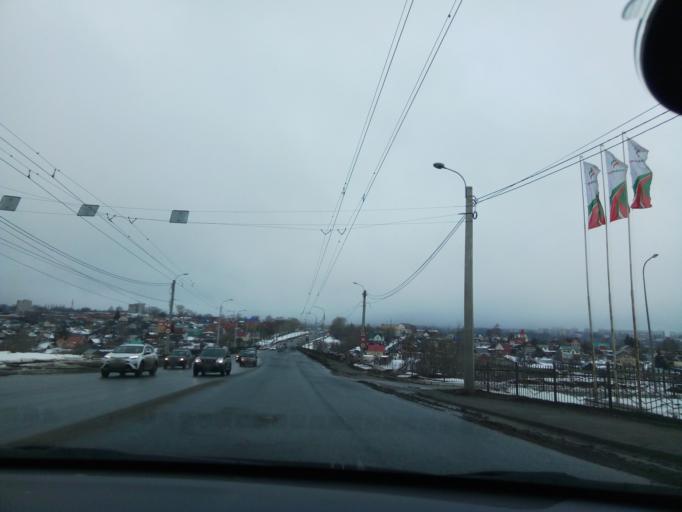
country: RU
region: Chuvashia
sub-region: Cheboksarskiy Rayon
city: Cheboksary
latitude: 56.1249
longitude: 47.2223
